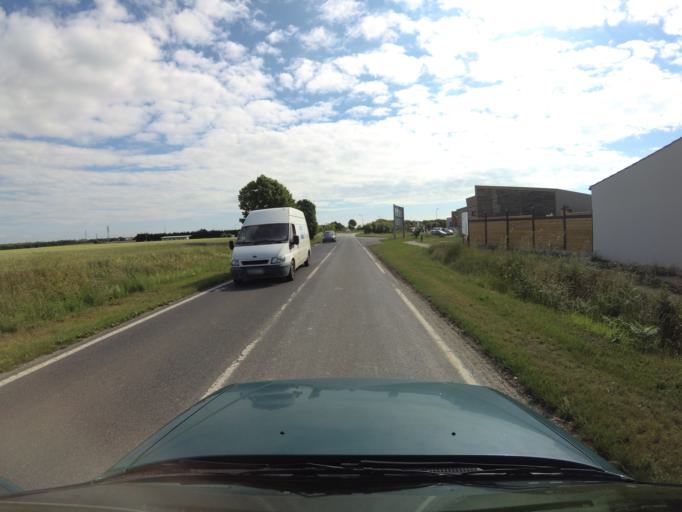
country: FR
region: Poitou-Charentes
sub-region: Departement de la Charente-Maritime
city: Saint-Xandre
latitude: 46.2358
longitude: -1.0724
